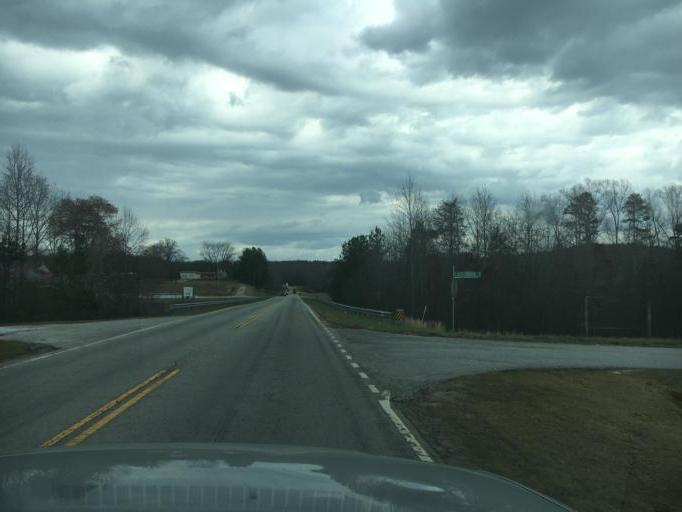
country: US
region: South Carolina
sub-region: Oconee County
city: Walhalla
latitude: 34.7377
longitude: -83.0522
